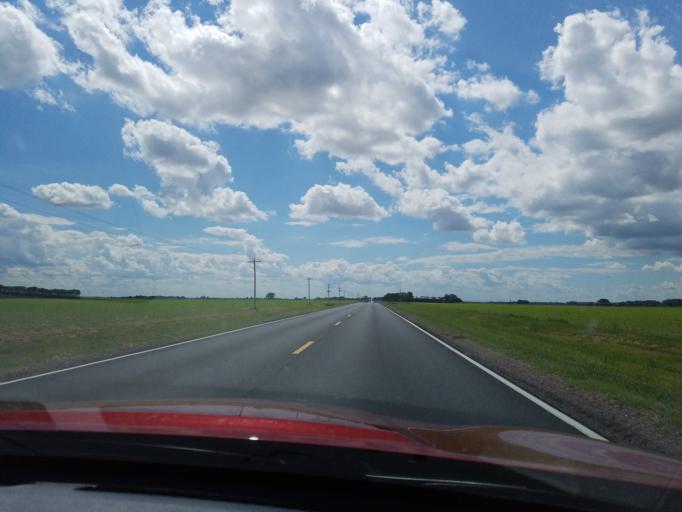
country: US
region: Nebraska
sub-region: Buffalo County
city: Kearney
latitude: 40.6411
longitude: -99.0476
